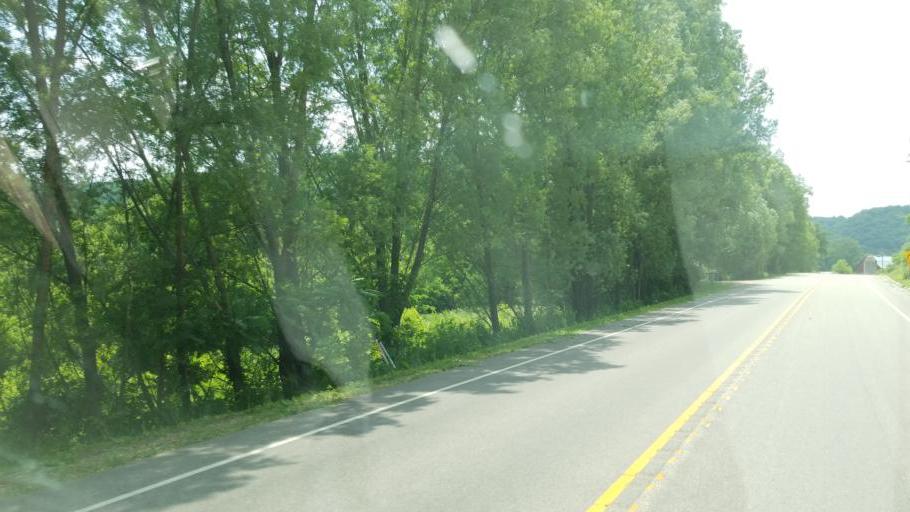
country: US
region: Wisconsin
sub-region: Vernon County
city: Viroqua
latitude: 43.4676
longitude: -90.7119
